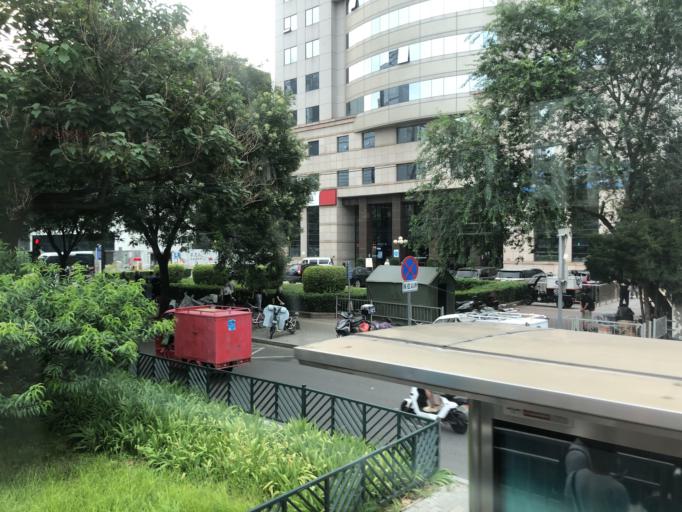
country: CN
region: Beijing
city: Jinrongjie
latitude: 39.9312
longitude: 116.3161
